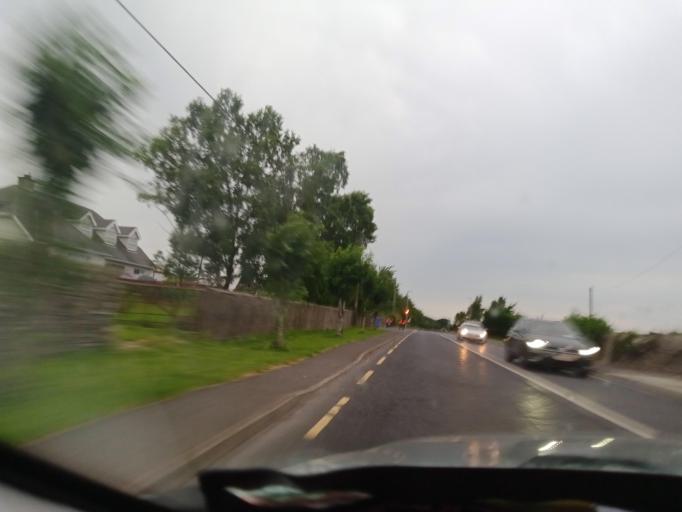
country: IE
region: Leinster
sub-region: Laois
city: Mountmellick
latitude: 53.1352
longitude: -7.4094
